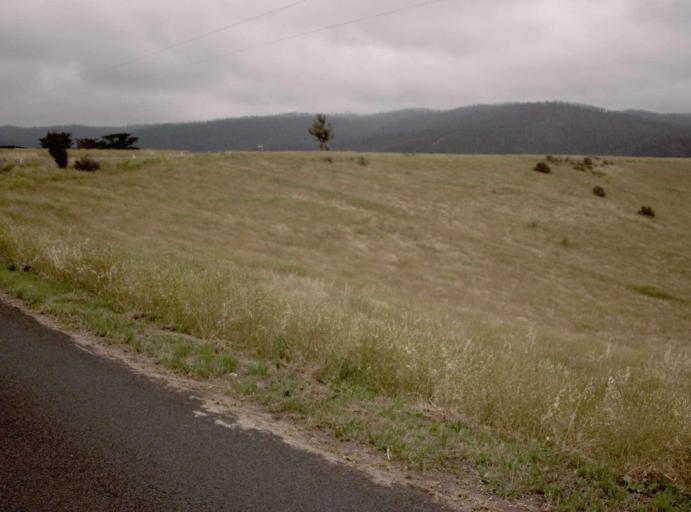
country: AU
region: Victoria
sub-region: Wellington
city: Heyfield
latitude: -37.8384
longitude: 146.6880
